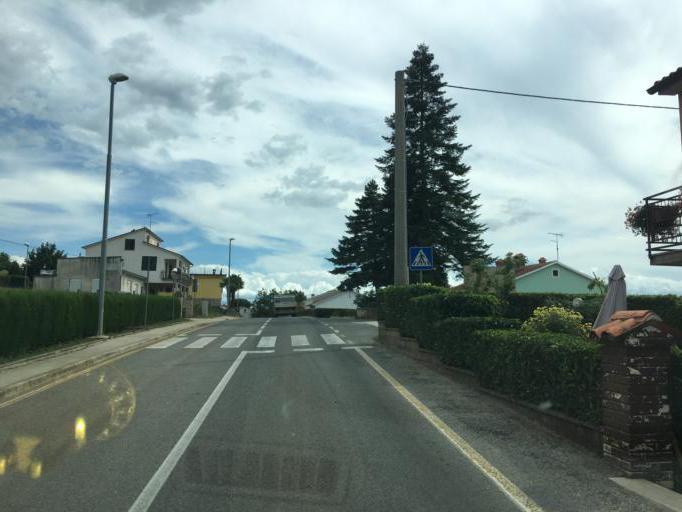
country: HR
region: Istarska
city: Karojba
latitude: 45.2585
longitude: 13.8712
